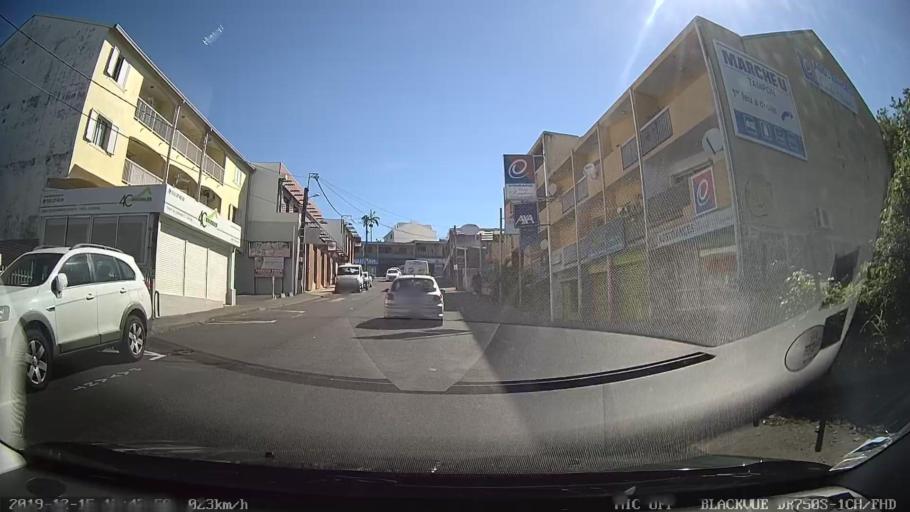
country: RE
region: Reunion
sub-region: Reunion
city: Le Tampon
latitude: -21.2794
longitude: 55.5147
